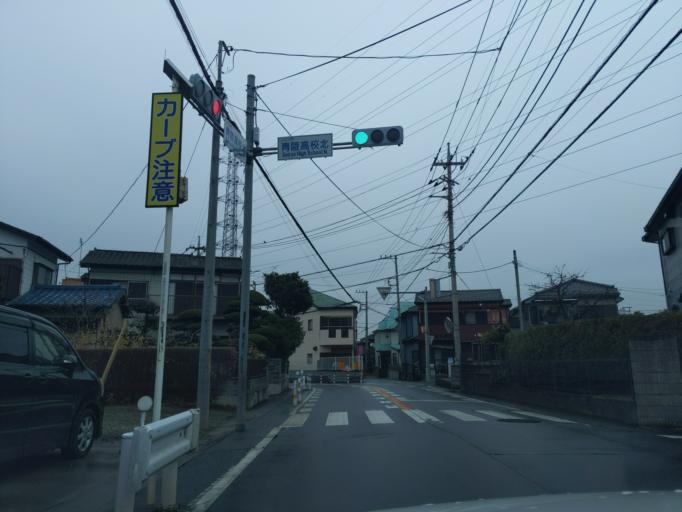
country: JP
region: Saitama
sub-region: Kawaguchi-shi
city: Hatogaya-honcho
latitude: 35.8582
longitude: 139.7286
